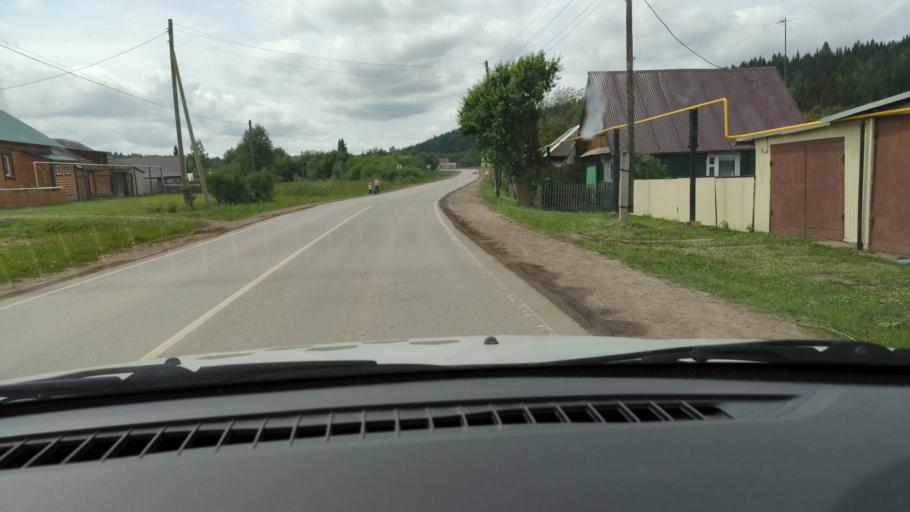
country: RU
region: Perm
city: Kukushtan
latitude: 57.4499
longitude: 56.5163
